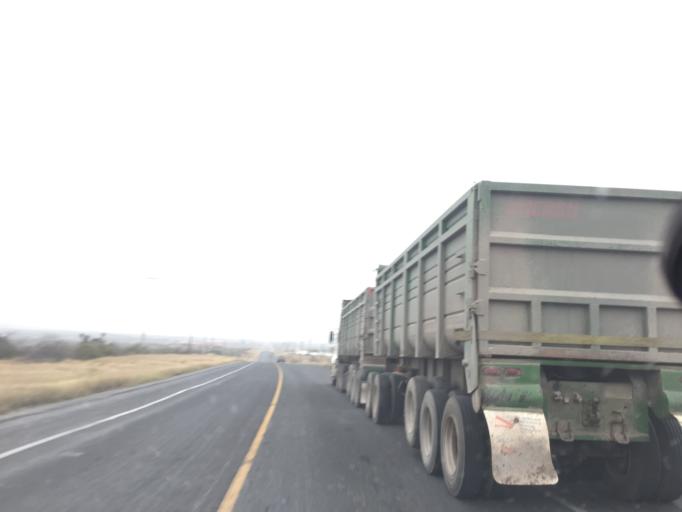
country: MX
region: Nuevo Leon
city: Mina
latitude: 25.9983
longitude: -100.4677
